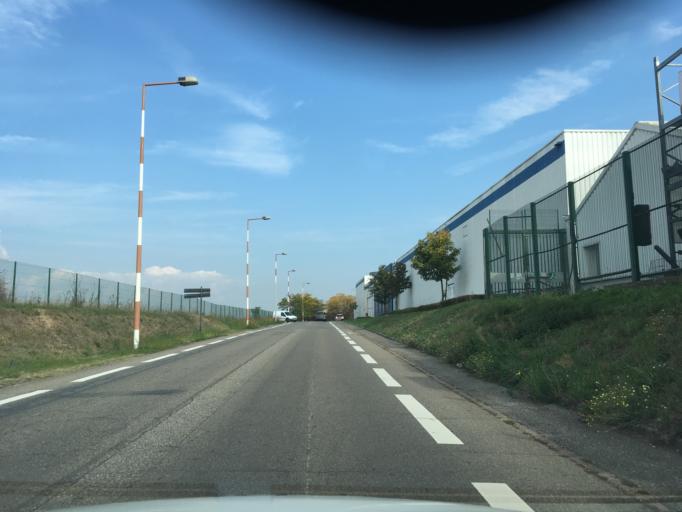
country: FR
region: Alsace
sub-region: Departement du Haut-Rhin
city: Colmar
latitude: 48.1041
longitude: 7.3611
